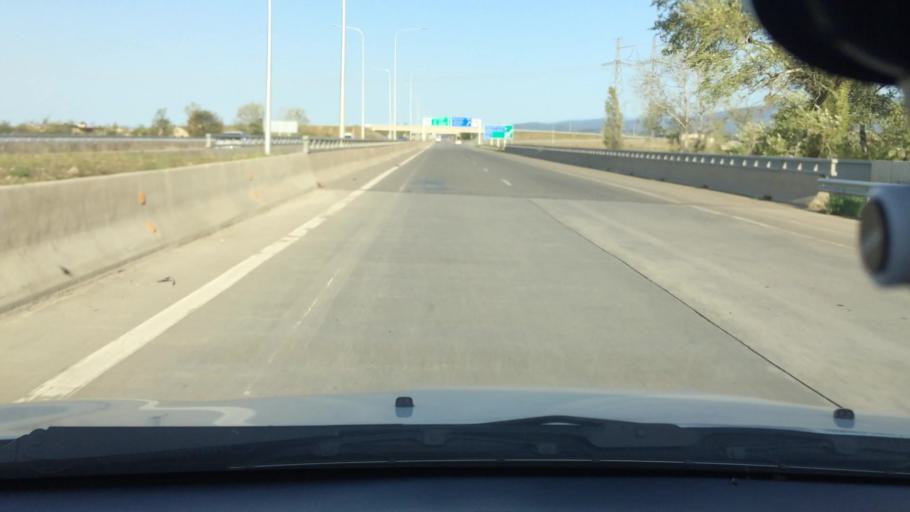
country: GE
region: Imereti
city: Zestap'oni
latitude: 42.1560
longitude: 42.9547
